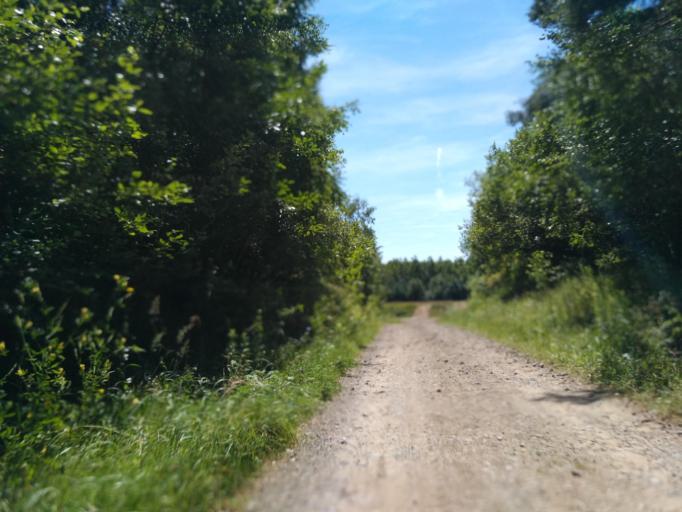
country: PL
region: Subcarpathian Voivodeship
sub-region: Powiat sanocki
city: Bukowsko
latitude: 49.4808
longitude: 22.0921
